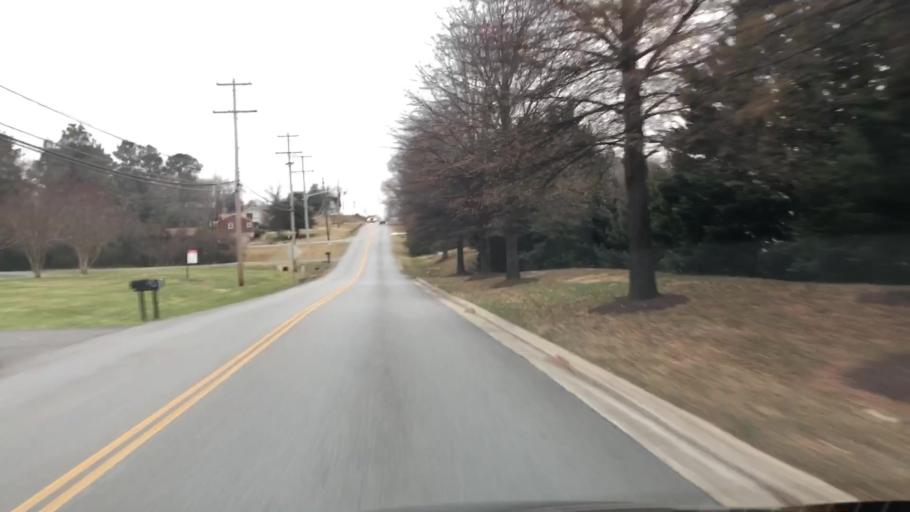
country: US
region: Virginia
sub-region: City of Lynchburg
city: West Lynchburg
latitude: 37.3454
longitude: -79.1922
